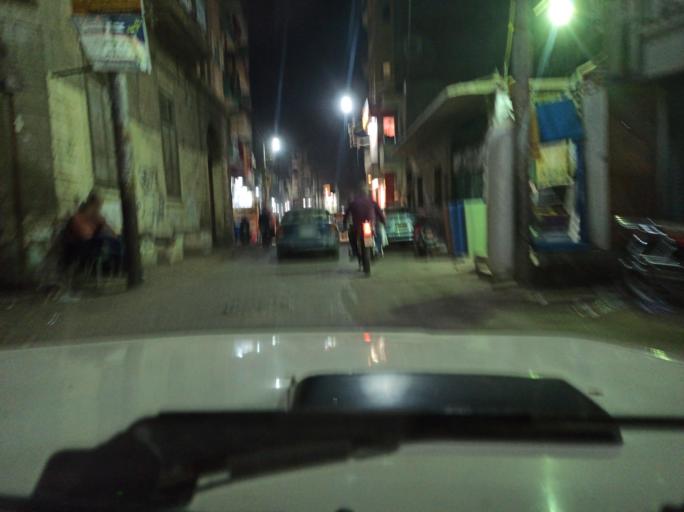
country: EG
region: Muhafazat Bani Suwayf
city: Bani Suwayf
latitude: 29.0735
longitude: 31.0934
